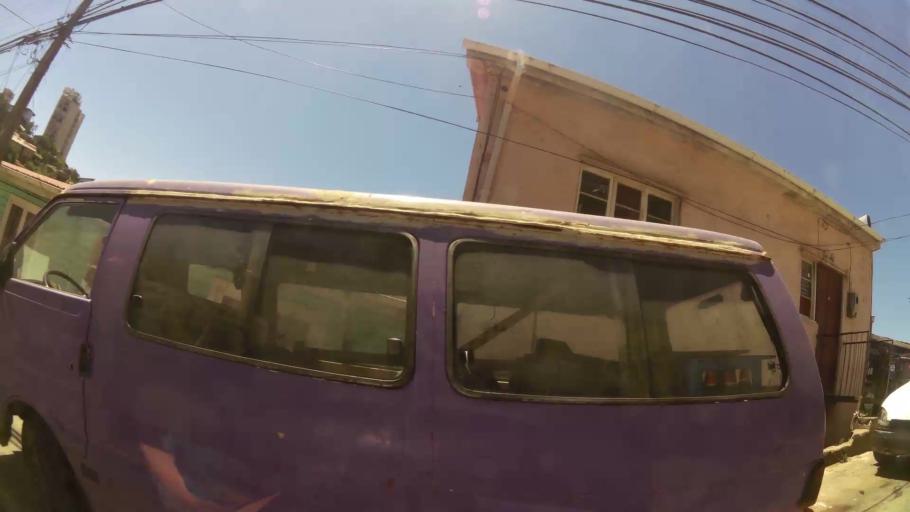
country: CL
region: Valparaiso
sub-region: Provincia de Valparaiso
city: Valparaiso
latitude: -33.0530
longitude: -71.6330
